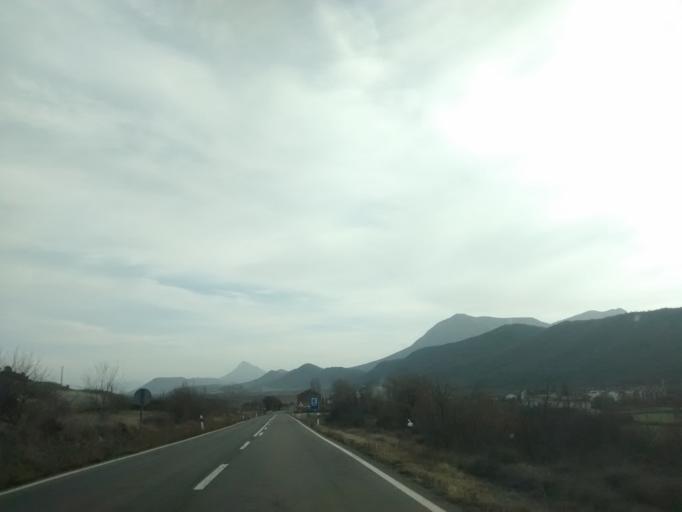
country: ES
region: Aragon
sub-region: Provincia de Huesca
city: Bailo
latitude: 42.5630
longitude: -0.7946
